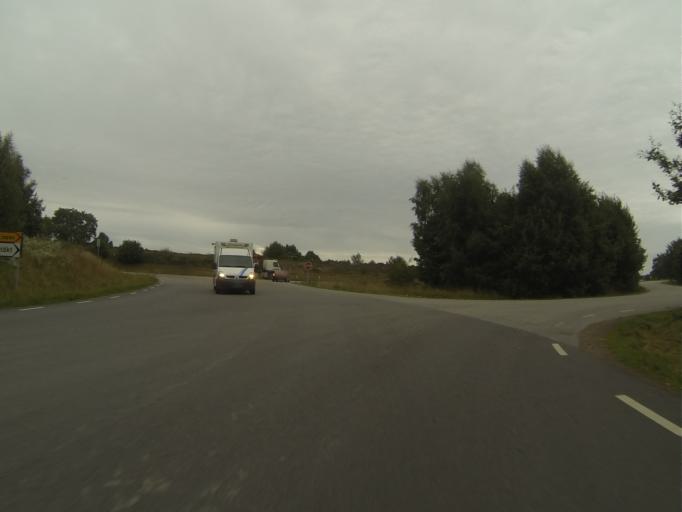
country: SE
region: Skane
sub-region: Lunds Kommun
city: Veberod
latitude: 55.6479
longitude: 13.4550
